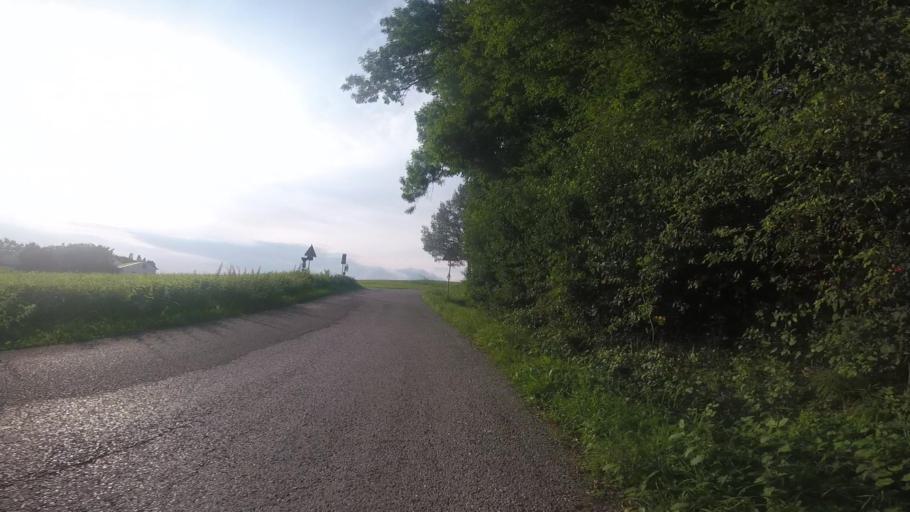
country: DE
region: Baden-Wuerttemberg
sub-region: Regierungsbezirk Stuttgart
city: Aspach
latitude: 49.0032
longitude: 9.3818
